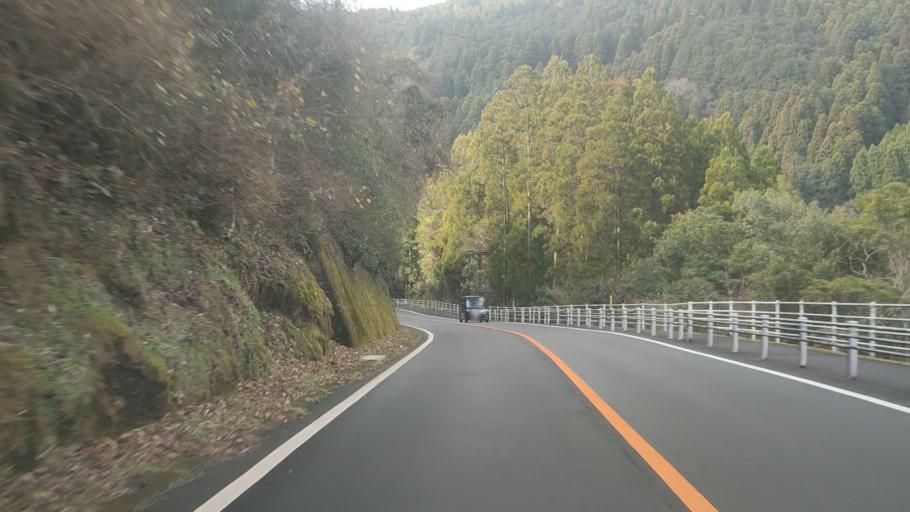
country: JP
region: Kumamoto
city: Hitoyoshi
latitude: 32.2928
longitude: 130.8434
